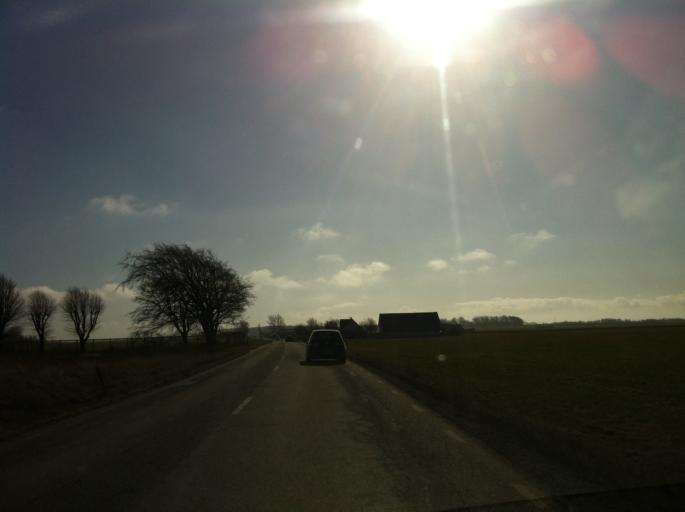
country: SE
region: Skane
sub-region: Bastads Kommun
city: Forslov
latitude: 56.3158
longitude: 12.8383
